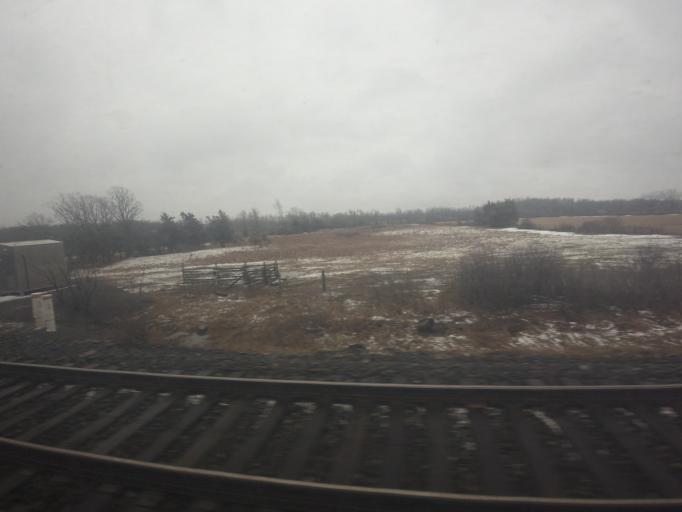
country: CA
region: Ontario
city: Deseronto
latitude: 44.2178
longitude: -77.1603
